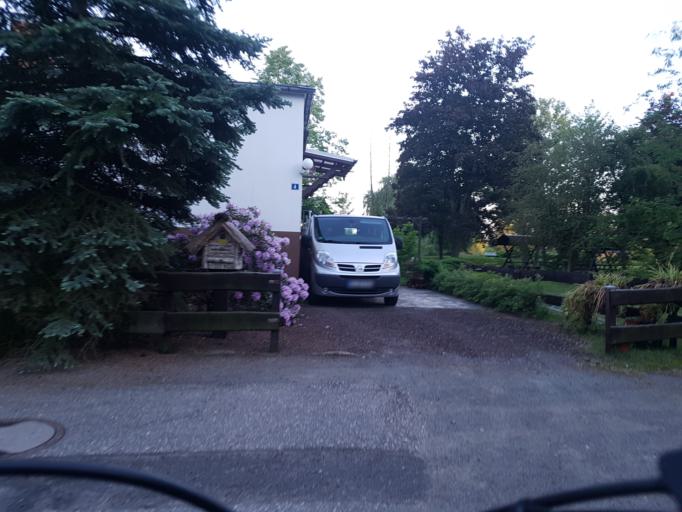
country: DE
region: Brandenburg
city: Bad Liebenwerda
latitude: 51.5474
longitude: 13.3708
